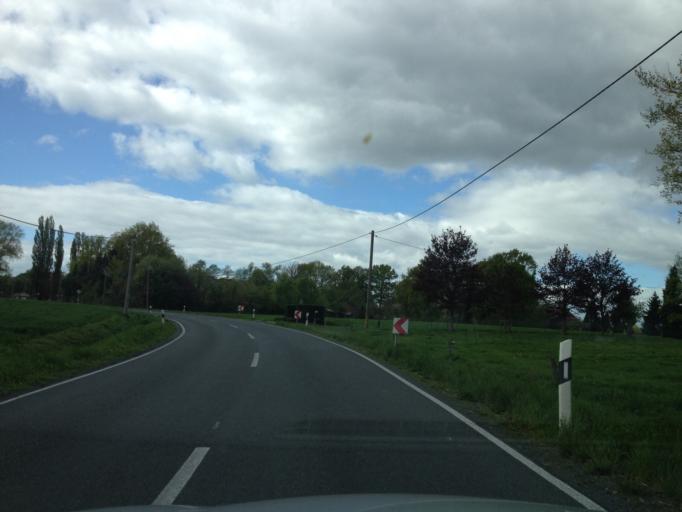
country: DE
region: North Rhine-Westphalia
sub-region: Regierungsbezirk Detmold
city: Verl
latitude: 51.8147
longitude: 8.5133
